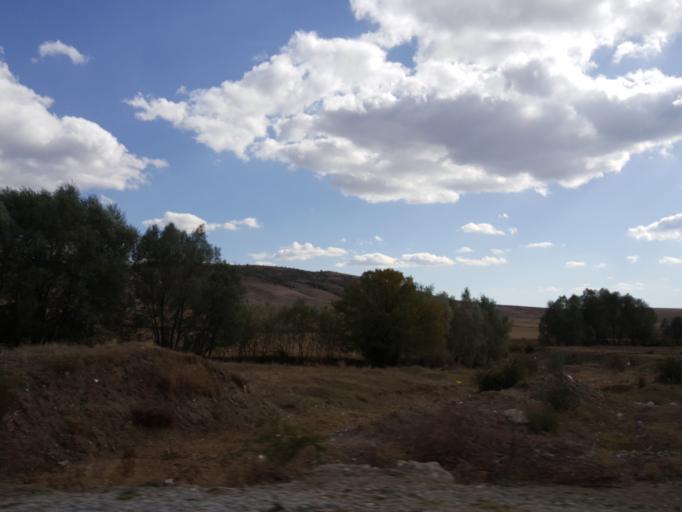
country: TR
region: Tokat
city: Sulusaray
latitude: 39.9863
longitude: 35.9530
